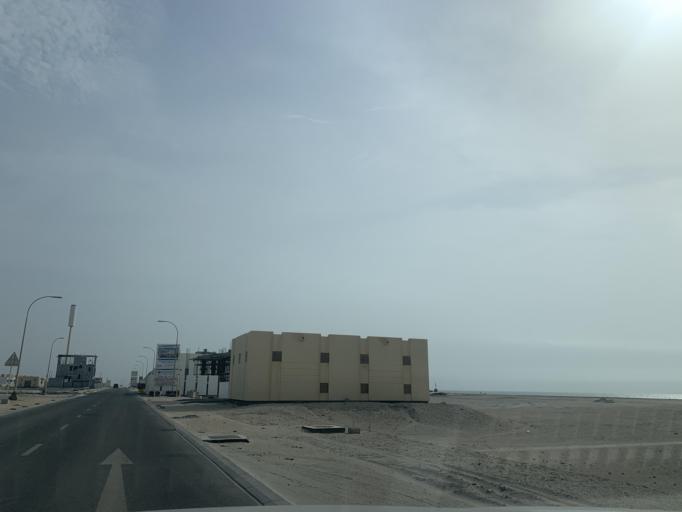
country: BH
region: Muharraq
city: Al Muharraq
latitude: 26.3201
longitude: 50.6224
